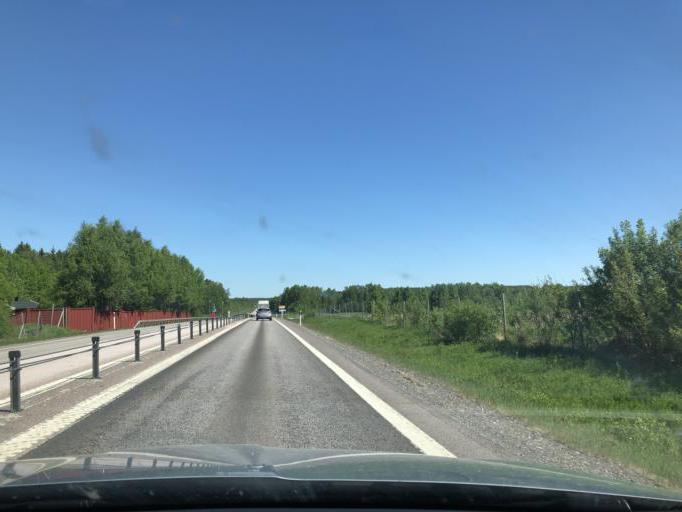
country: SE
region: Norrbotten
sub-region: Lulea Kommun
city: Lulea
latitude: 65.7251
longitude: 22.1499
